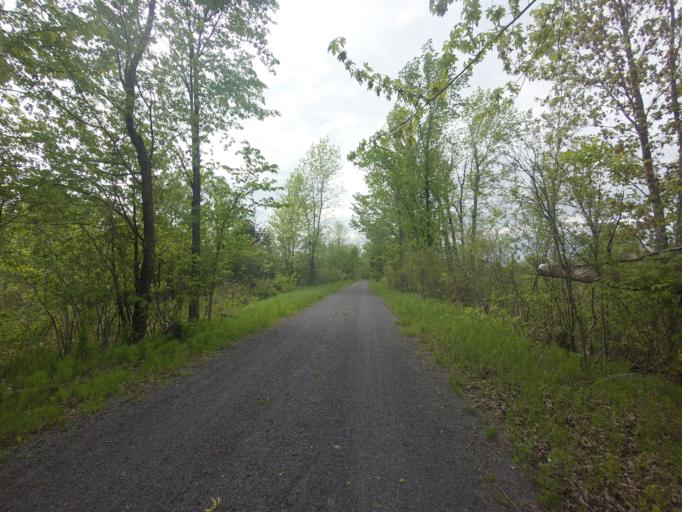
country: CA
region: Ontario
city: Kingston
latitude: 44.3721
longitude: -76.6364
